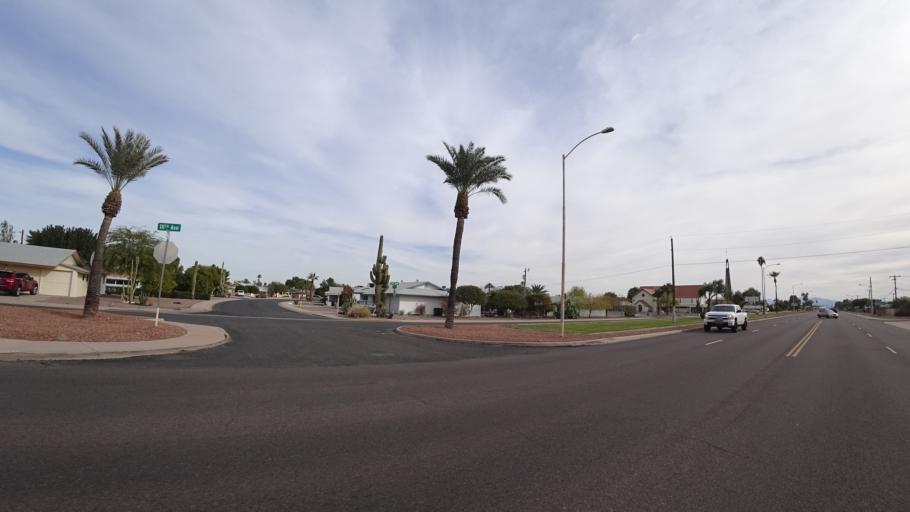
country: US
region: Arizona
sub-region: Maricopa County
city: Youngtown
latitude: 33.5861
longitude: -112.2988
